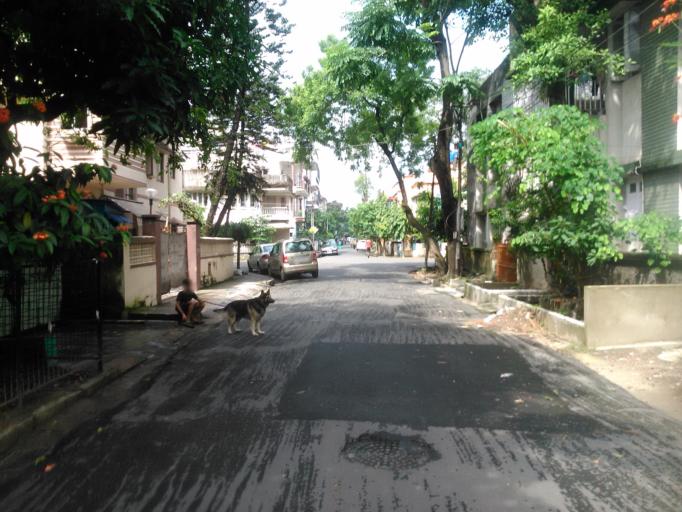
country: IN
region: West Bengal
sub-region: North 24 Parganas
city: Garui
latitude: 22.5957
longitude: 88.4079
